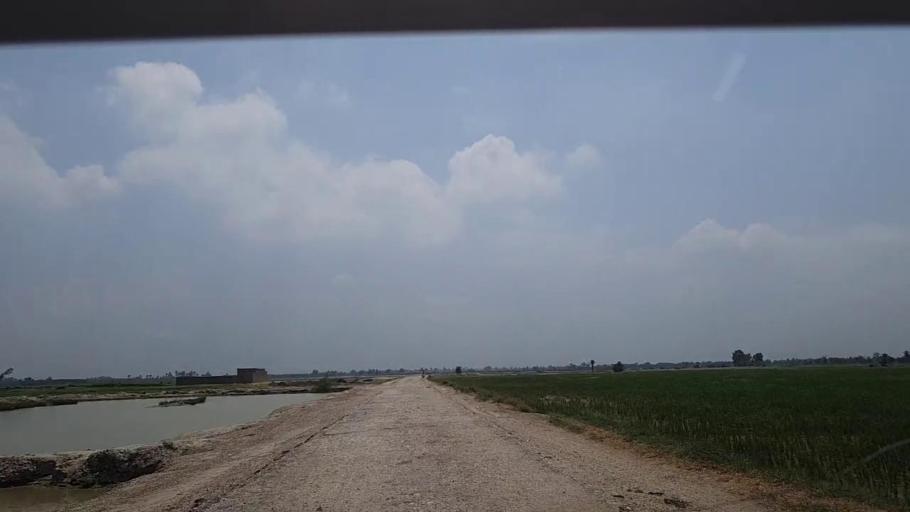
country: PK
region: Sindh
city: Khanpur
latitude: 27.9020
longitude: 69.3913
